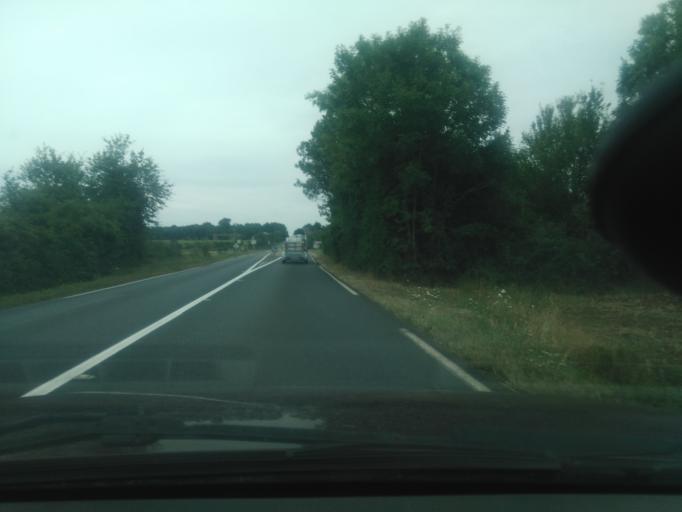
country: FR
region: Pays de la Loire
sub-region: Departement de la Vendee
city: Bazoges-en-Pareds
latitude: 46.6793
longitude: -0.9434
